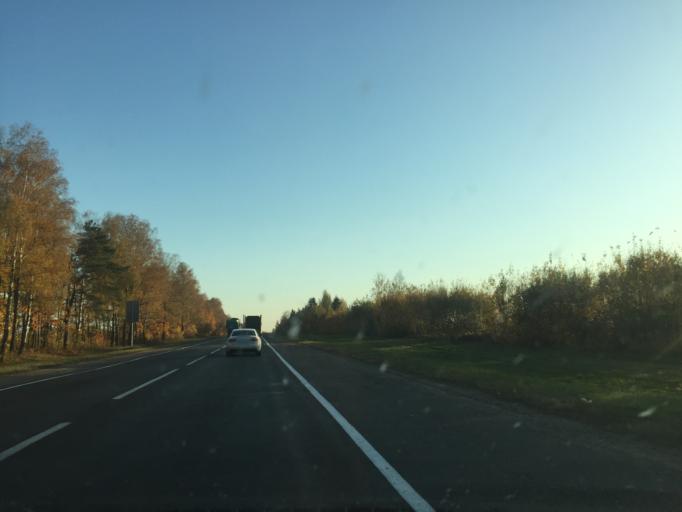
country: BY
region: Mogilev
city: Poselok Voskhod
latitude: 53.7526
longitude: 30.3653
